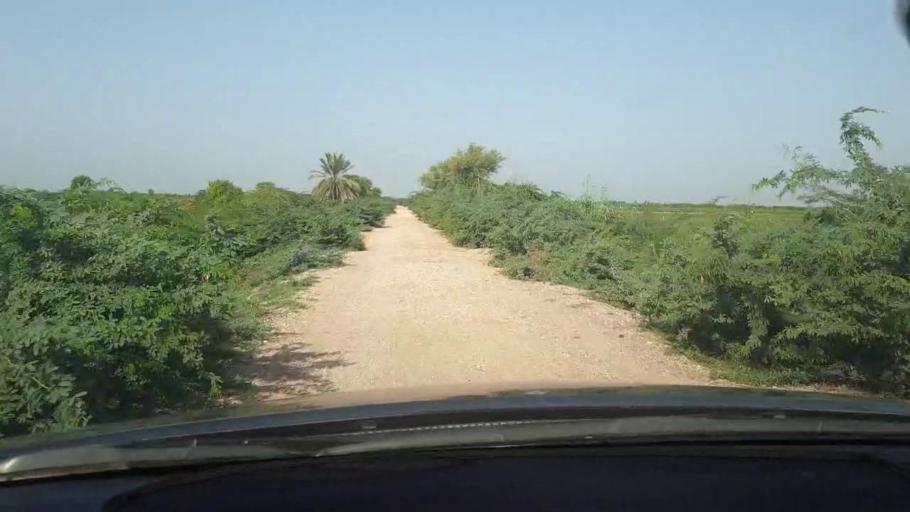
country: PK
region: Sindh
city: Tando Bago
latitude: 24.6799
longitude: 69.1556
